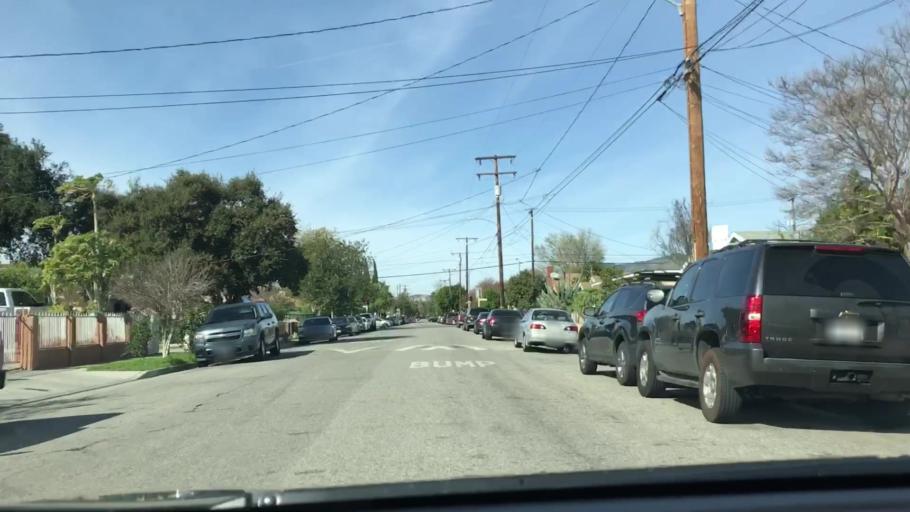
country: US
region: California
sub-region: Los Angeles County
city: San Fernando
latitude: 34.2795
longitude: -118.4449
